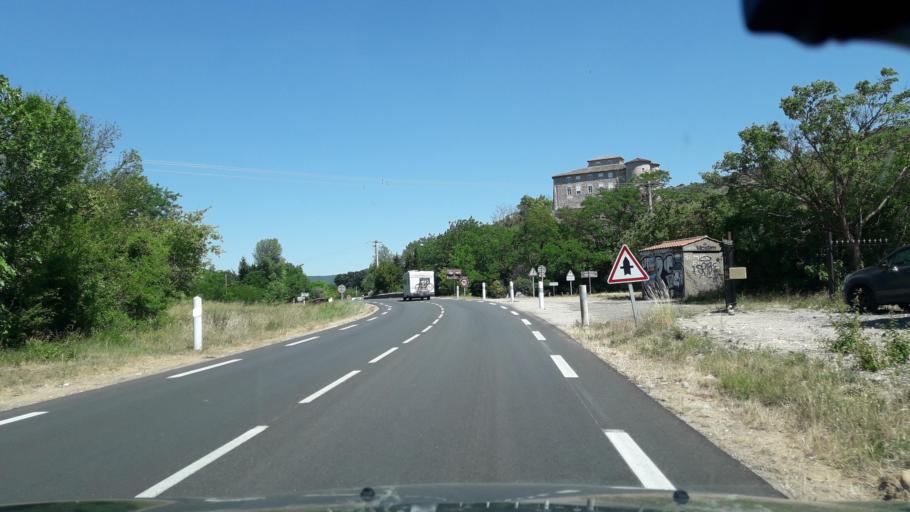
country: FR
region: Rhone-Alpes
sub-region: Departement de l'Ardeche
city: Ruoms
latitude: 44.4224
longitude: 4.3188
